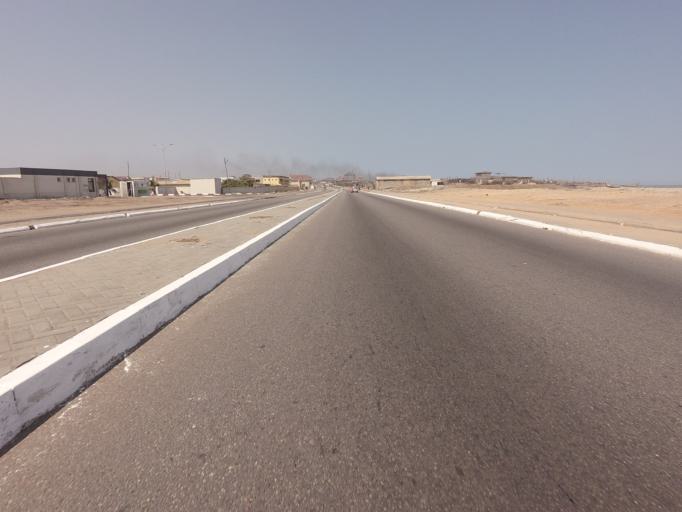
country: GH
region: Greater Accra
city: Accra
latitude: 5.5315
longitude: -0.2185
